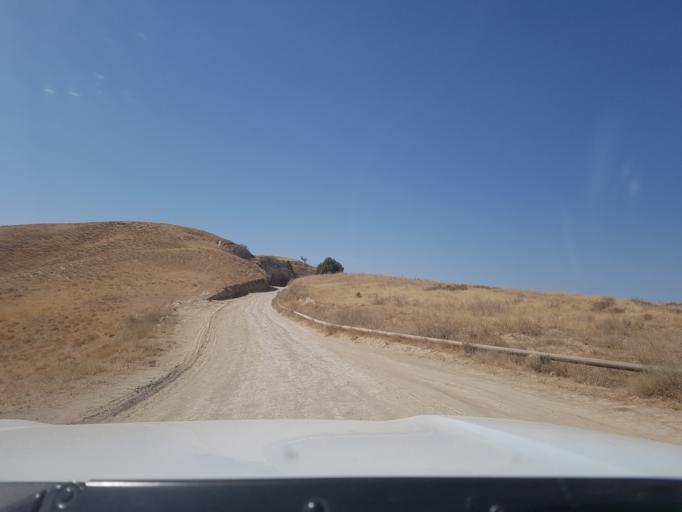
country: TM
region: Ahal
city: Baharly
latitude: 38.2766
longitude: 56.9118
